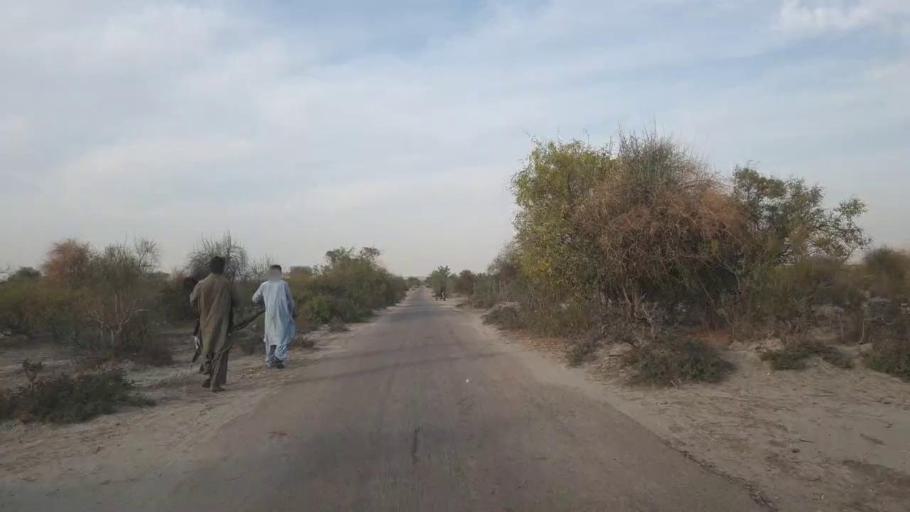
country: PK
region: Sindh
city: Nabisar
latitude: 25.1065
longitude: 69.6764
